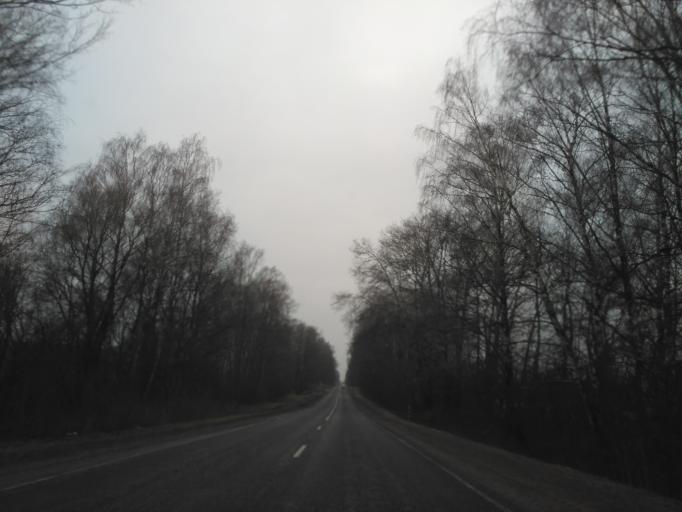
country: BY
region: Minsk
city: Snow
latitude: 53.2387
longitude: 26.2377
